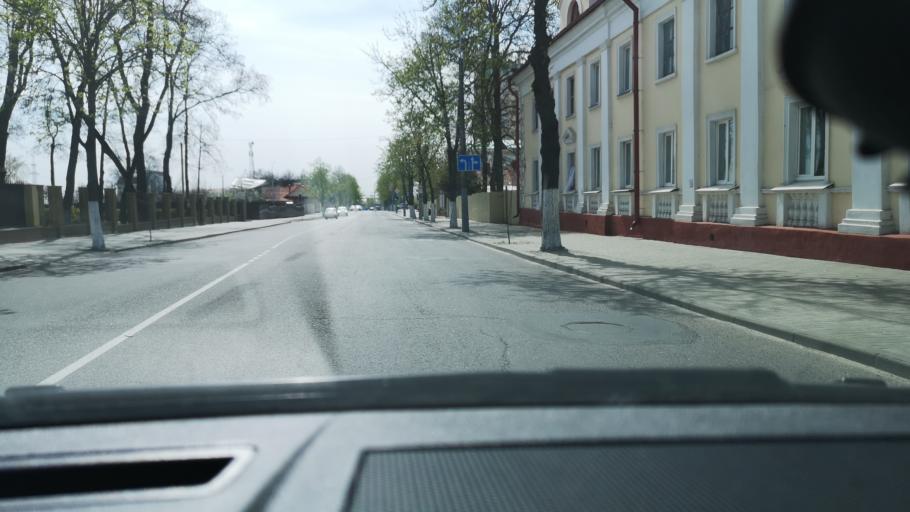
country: BY
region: Gomel
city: Gomel
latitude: 52.4174
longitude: 31.0078
